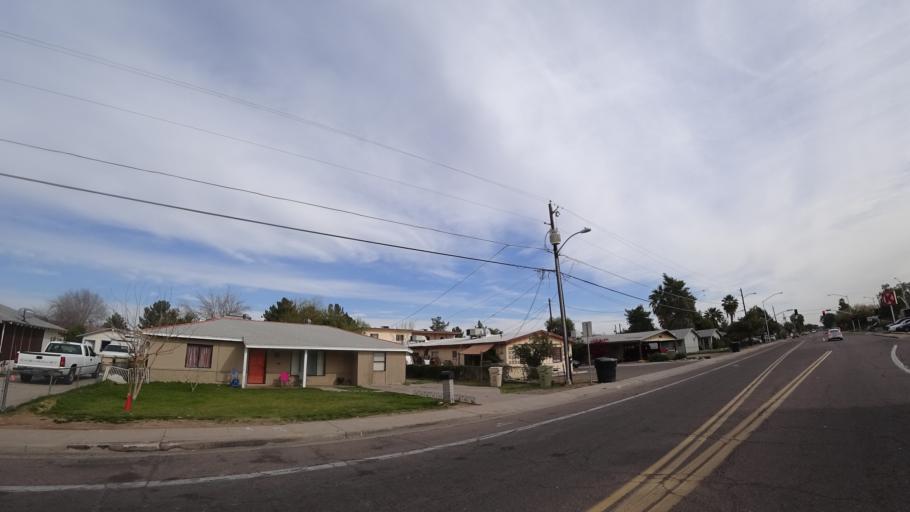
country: US
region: Arizona
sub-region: Maricopa County
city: Glendale
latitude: 33.5312
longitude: -112.1963
